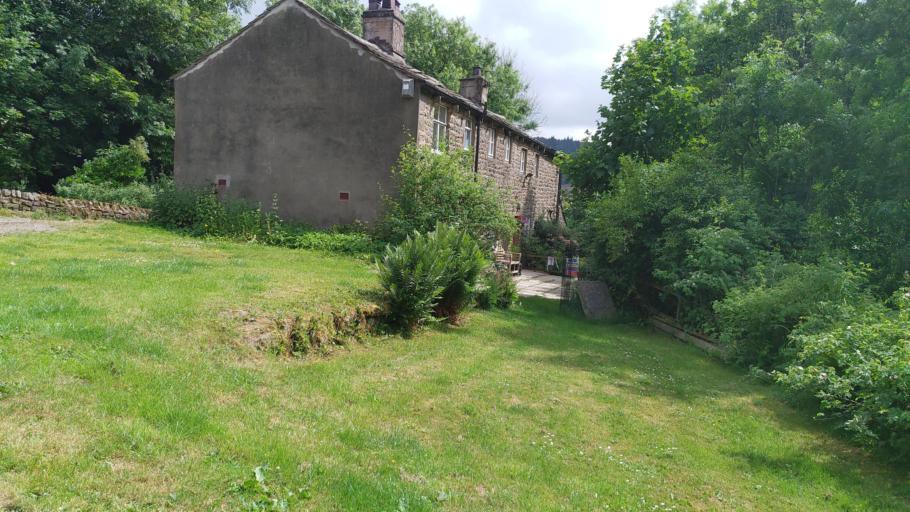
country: GB
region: England
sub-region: Lancashire
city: Padiham
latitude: 53.8358
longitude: -2.3348
